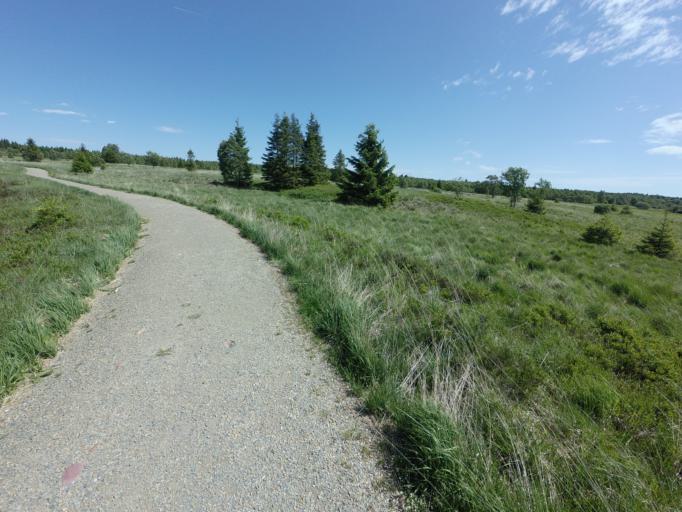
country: BE
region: Wallonia
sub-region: Province de Liege
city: Malmedy
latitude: 50.5079
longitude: 6.0690
